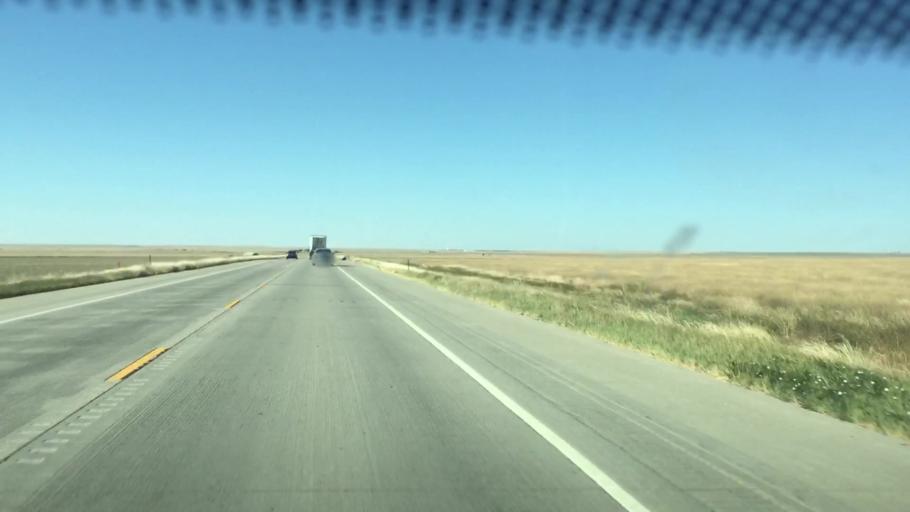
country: US
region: Colorado
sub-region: Kiowa County
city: Eads
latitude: 38.3626
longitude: -102.7214
